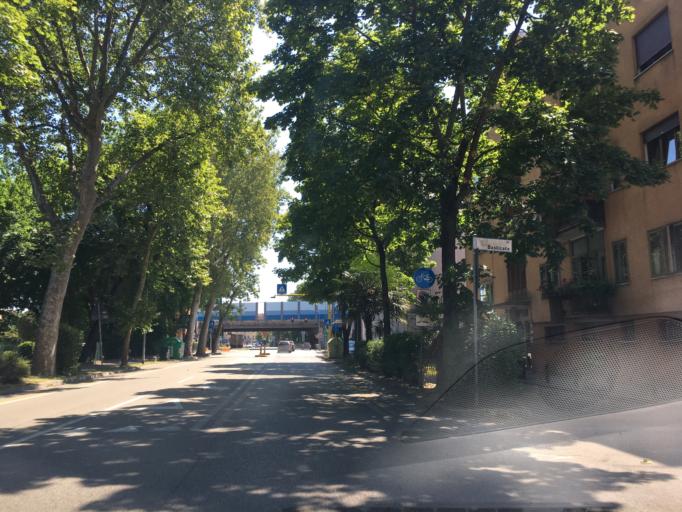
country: IT
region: Veneto
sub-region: Provincia di Venezia
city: Mestre
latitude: 45.4856
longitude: 12.2174
